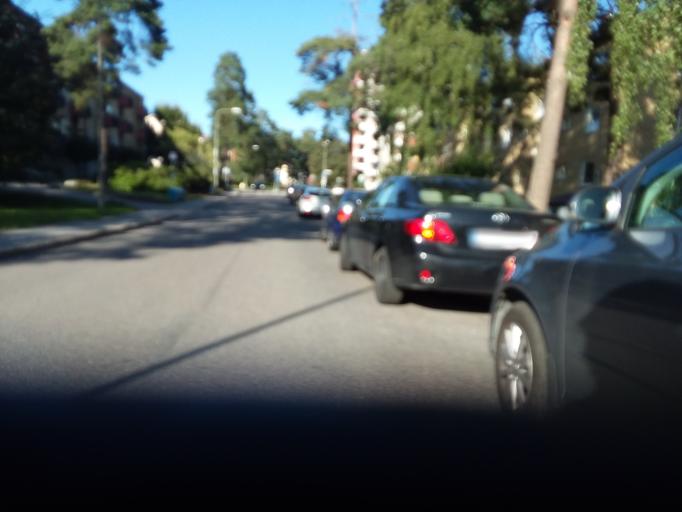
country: SE
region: Stockholm
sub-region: Stockholms Kommun
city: Bromma
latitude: 59.3480
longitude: 17.8780
